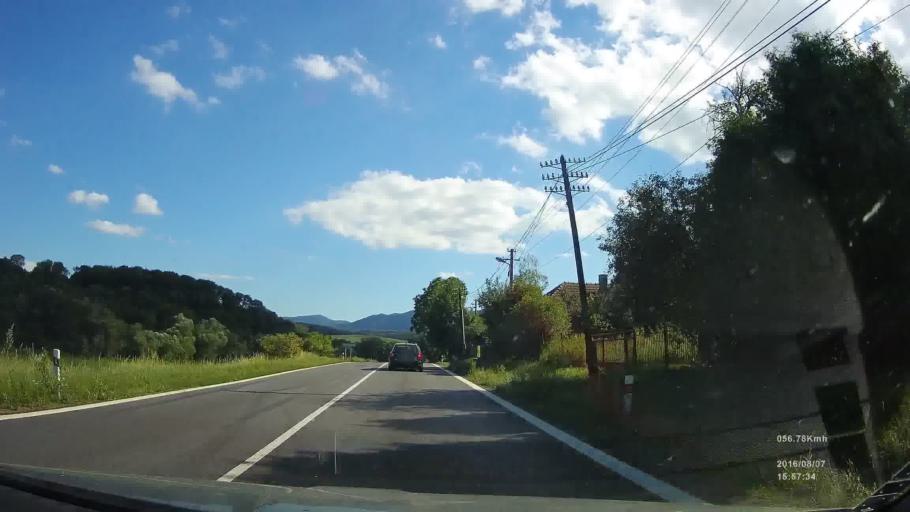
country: SK
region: Presovsky
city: Giraltovce
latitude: 49.0581
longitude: 21.4171
